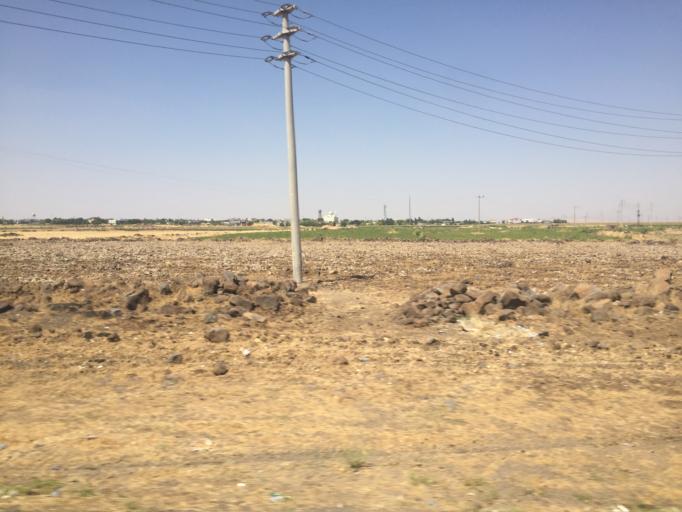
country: TR
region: Diyarbakir
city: Yolboyu
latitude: 37.8916
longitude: 40.0107
